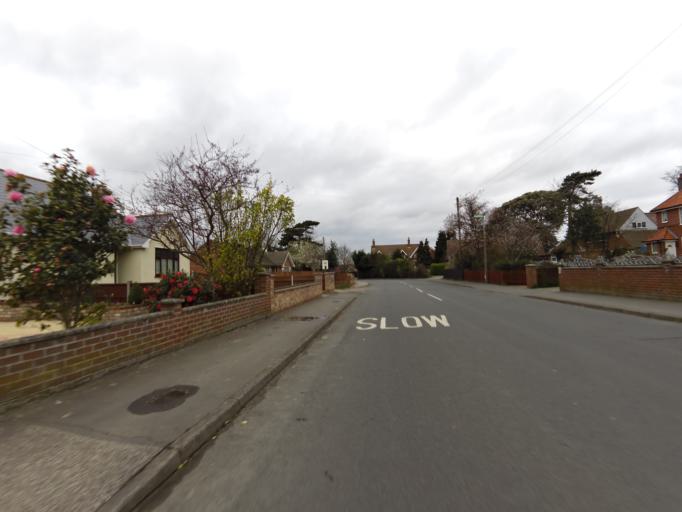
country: GB
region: England
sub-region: Norfolk
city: Hopton on Sea
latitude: 52.5128
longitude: 1.7433
